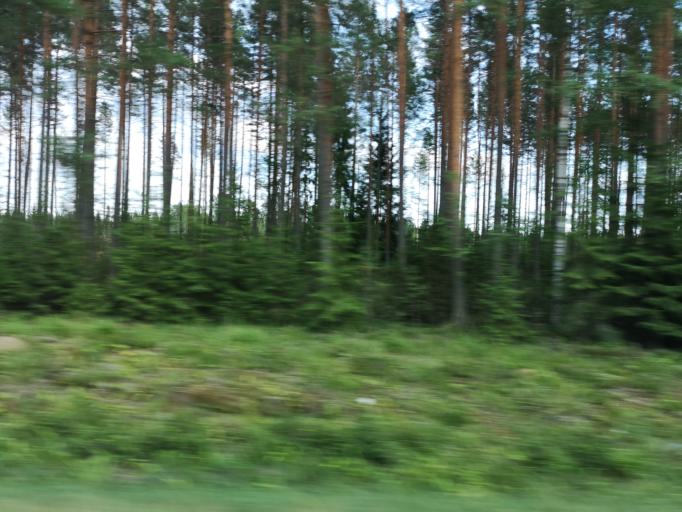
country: FI
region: Paijanne Tavastia
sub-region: Lahti
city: Hartola
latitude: 61.6689
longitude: 26.0383
